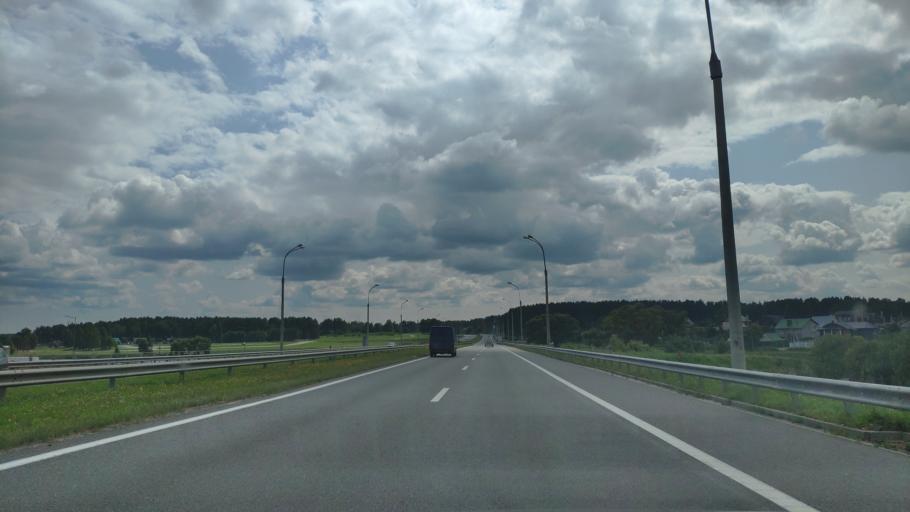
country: BY
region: Minsk
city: Zaslawye
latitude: 53.9998
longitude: 27.3073
